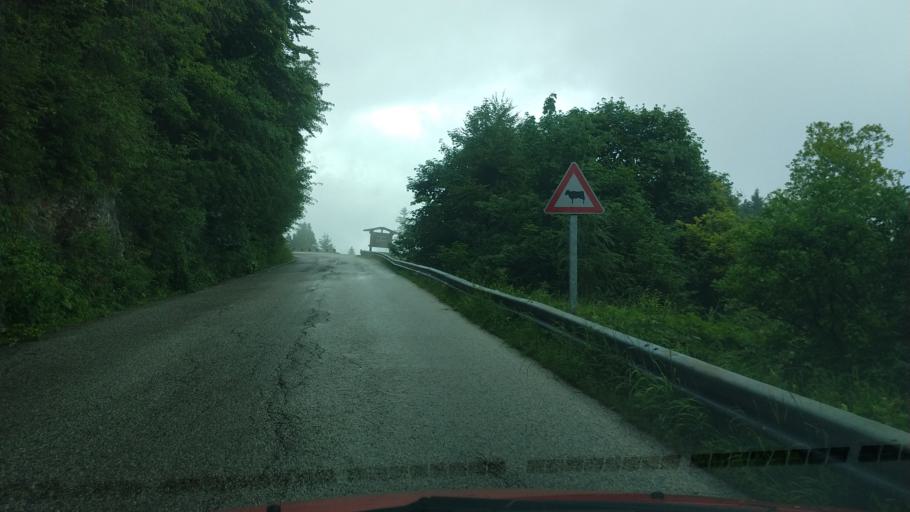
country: IT
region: Veneto
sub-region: Provincia di Vicenza
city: Longhi
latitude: 45.8774
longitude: 11.3052
